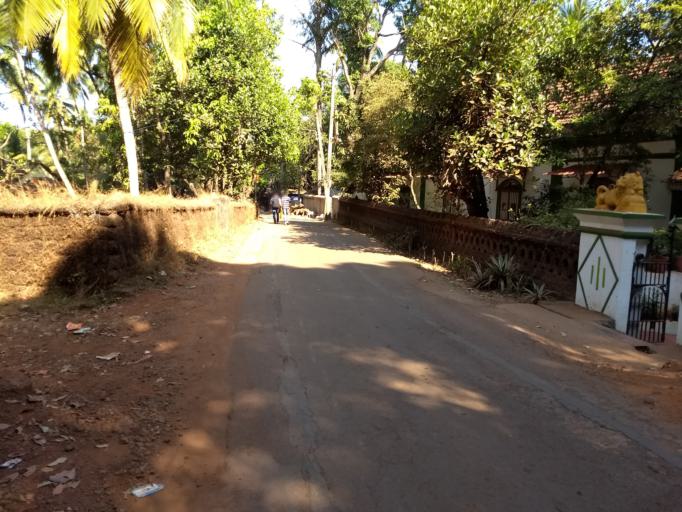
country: IN
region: Goa
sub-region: North Goa
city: Vagator
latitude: 15.6005
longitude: 73.7396
